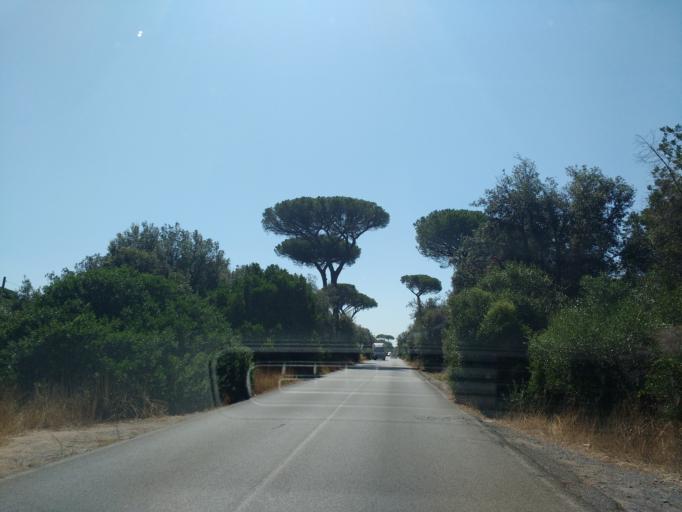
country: IT
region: Latium
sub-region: Citta metropolitana di Roma Capitale
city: Acilia-Castel Fusano-Ostia Antica
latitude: 41.7203
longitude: 12.3482
